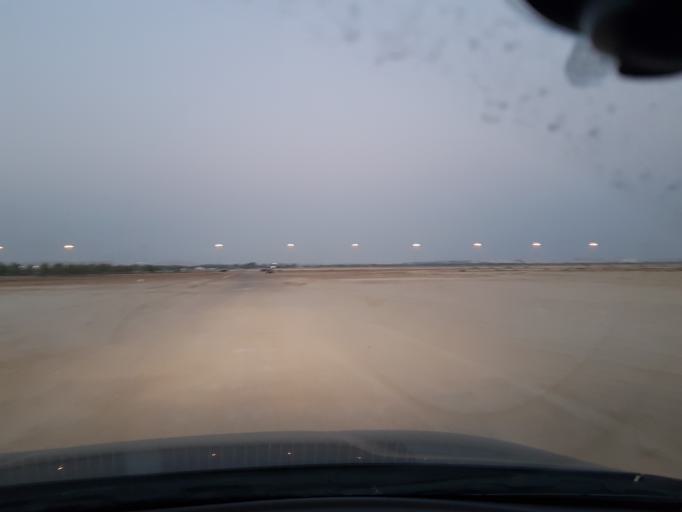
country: BH
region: Central Governorate
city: Dar Kulayb
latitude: 26.0101
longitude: 50.4803
